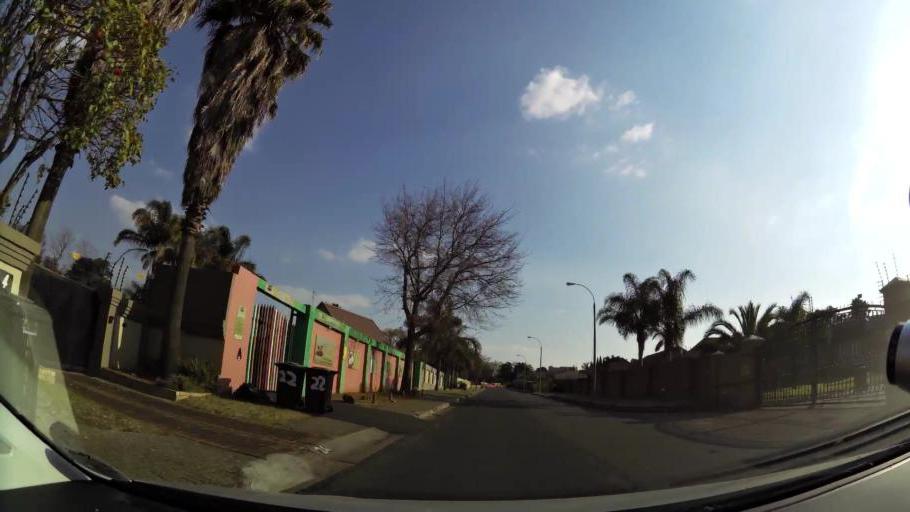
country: ZA
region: Gauteng
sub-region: City of Johannesburg Metropolitan Municipality
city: Modderfontein
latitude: -26.0770
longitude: 28.2081
